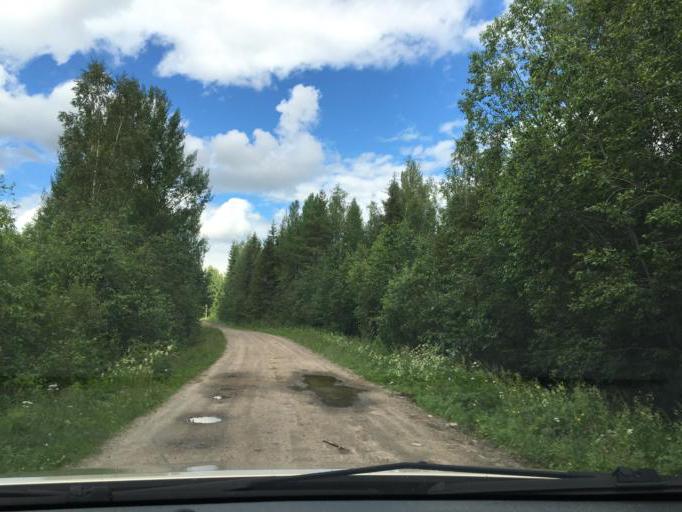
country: SE
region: Norrbotten
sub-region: Overkalix Kommun
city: OEverkalix
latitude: 66.1265
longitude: 22.7843
